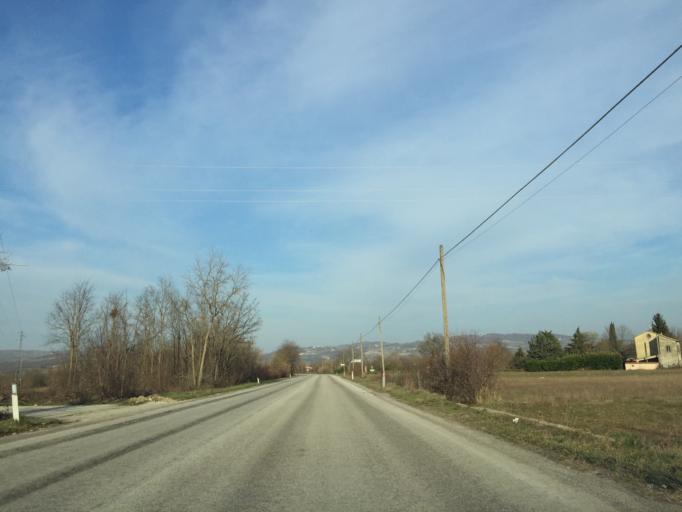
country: IT
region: Molise
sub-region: Provincia di Campobasso
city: San Massimo
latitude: 41.5048
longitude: 14.4259
